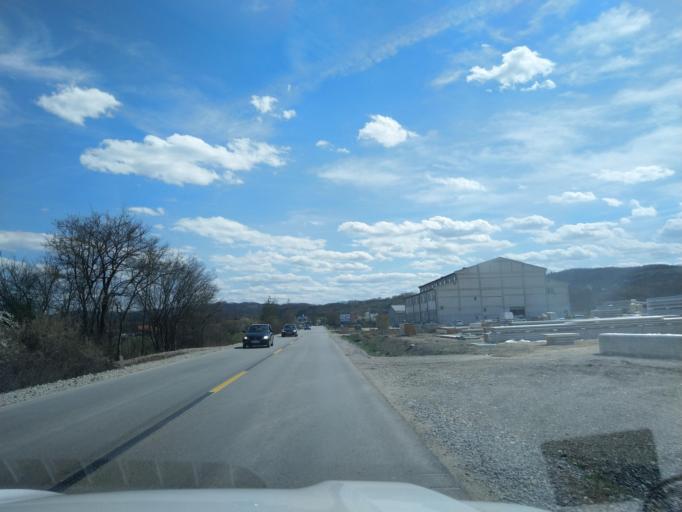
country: RS
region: Central Serbia
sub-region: Zlatiborski Okrug
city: Arilje
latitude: 43.7998
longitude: 20.0962
